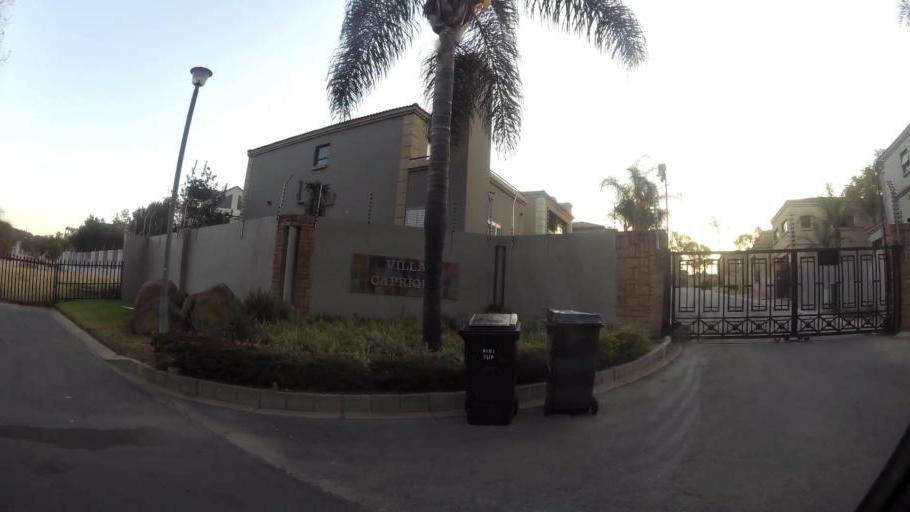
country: ZA
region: Gauteng
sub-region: City of Johannesburg Metropolitan Municipality
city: Diepsloot
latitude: -26.0236
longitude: 28.0328
